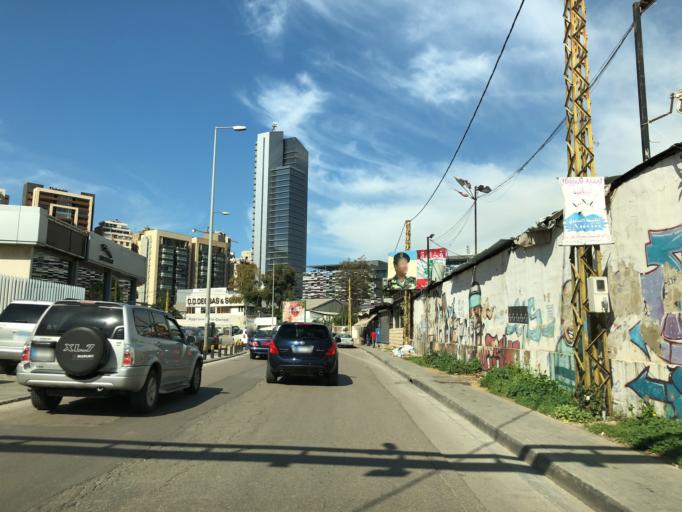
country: LB
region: Mont-Liban
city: Jdaidet el Matn
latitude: 33.8832
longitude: 35.5315
